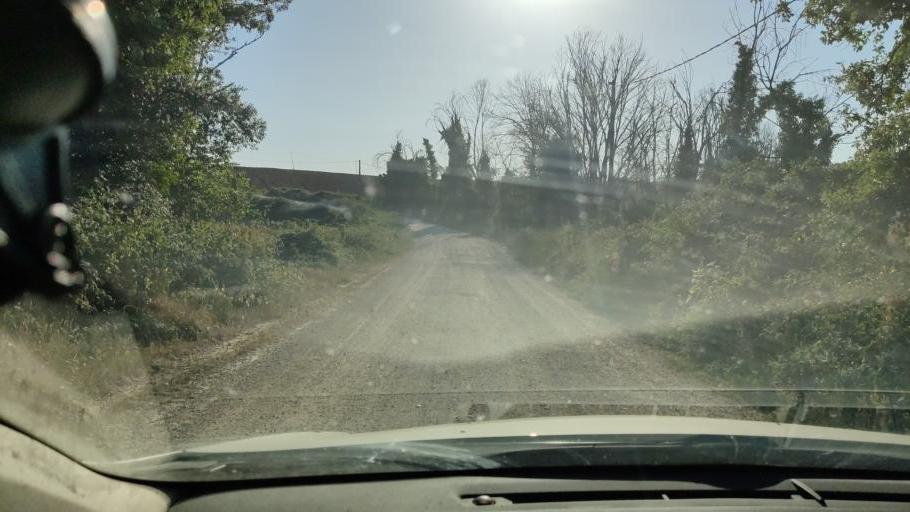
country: IT
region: Umbria
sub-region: Provincia di Terni
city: Giove
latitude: 42.5399
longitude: 12.3658
